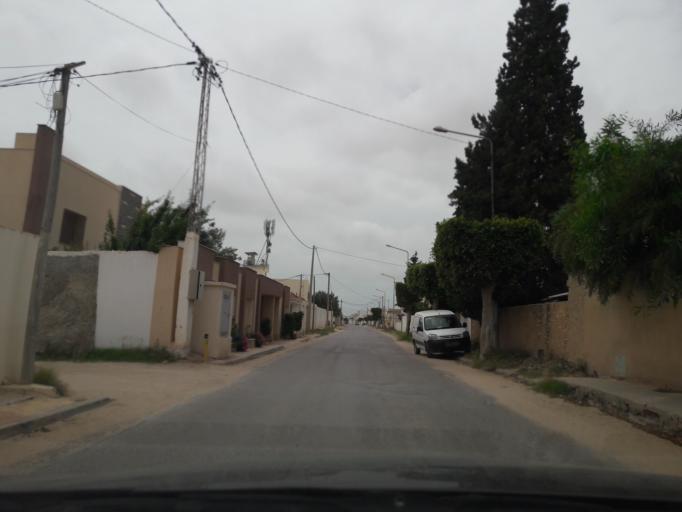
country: TN
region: Safaqis
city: Al Qarmadah
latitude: 34.7950
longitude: 10.7534
